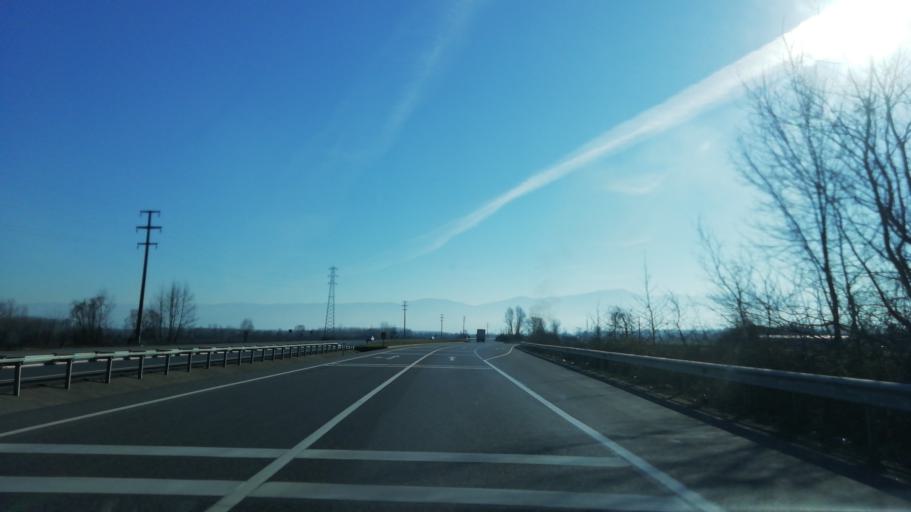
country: TR
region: Sakarya
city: Akyazi
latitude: 40.7361
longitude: 30.5647
